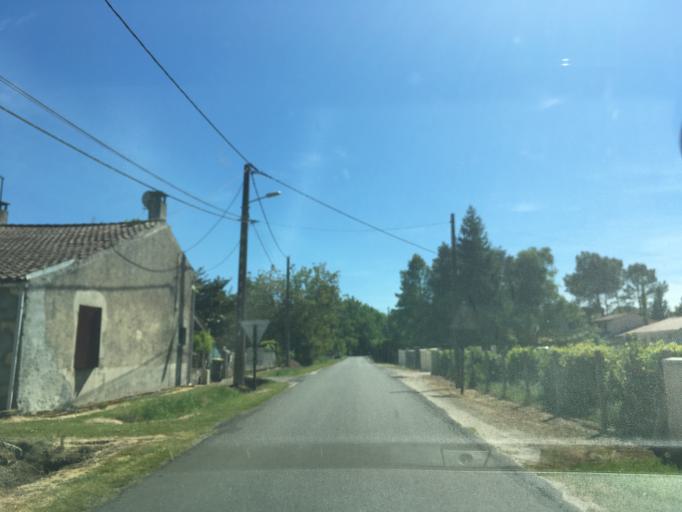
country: FR
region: Aquitaine
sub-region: Departement de la Gironde
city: Lesparre-Medoc
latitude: 45.2944
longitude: -0.8928
